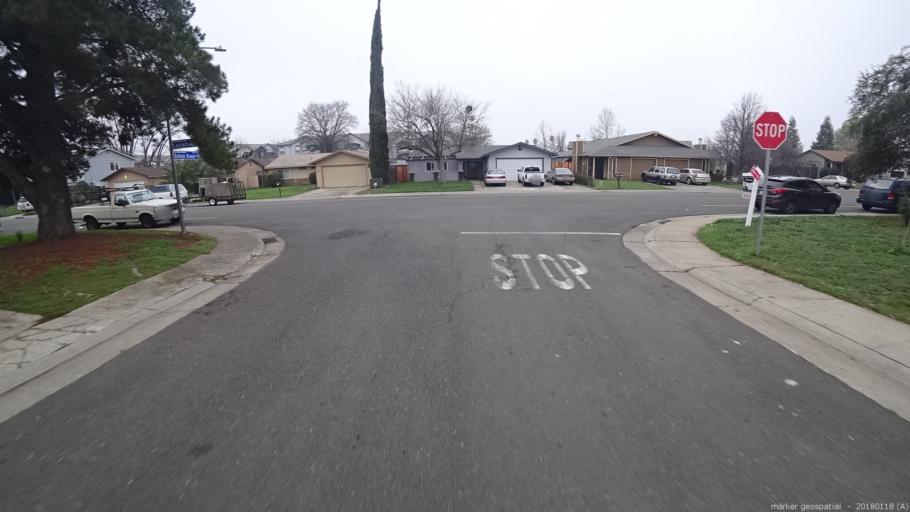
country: US
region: California
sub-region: Sacramento County
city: Rancho Cordova
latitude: 38.5791
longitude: -121.3036
